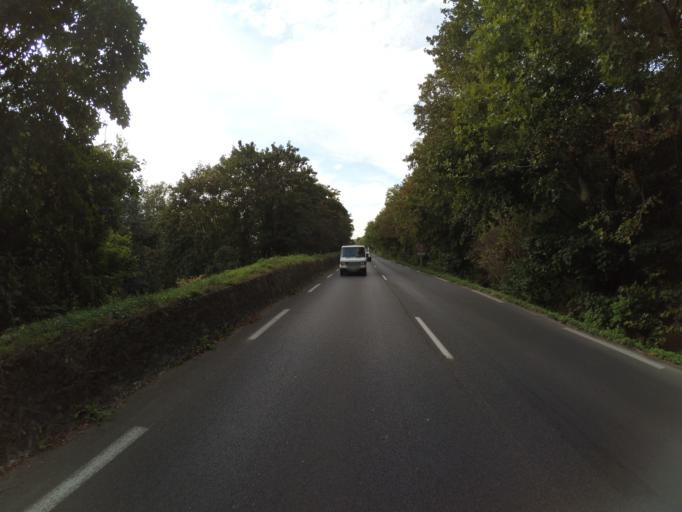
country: FR
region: Centre
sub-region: Departement d'Indre-et-Loire
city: Vouvray
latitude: 47.4103
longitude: 0.7842
